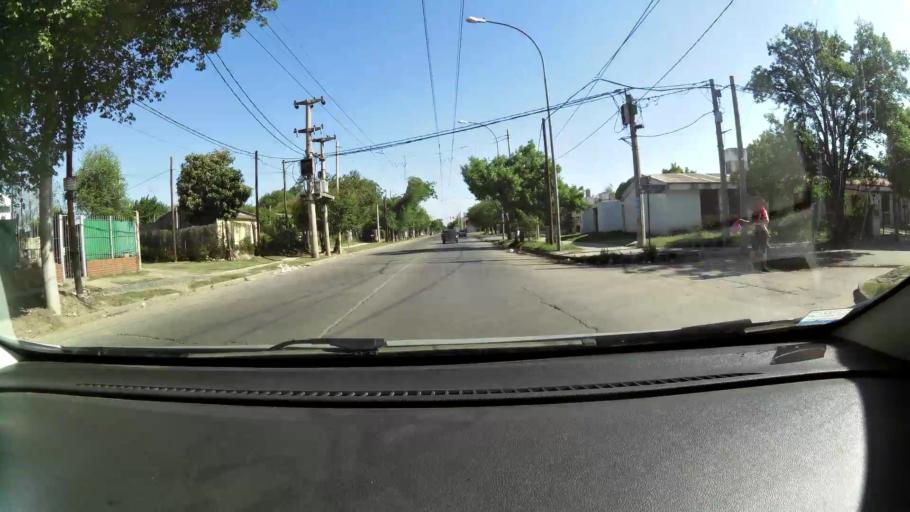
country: AR
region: Cordoba
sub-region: Departamento de Capital
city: Cordoba
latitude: -31.3759
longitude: -64.1839
